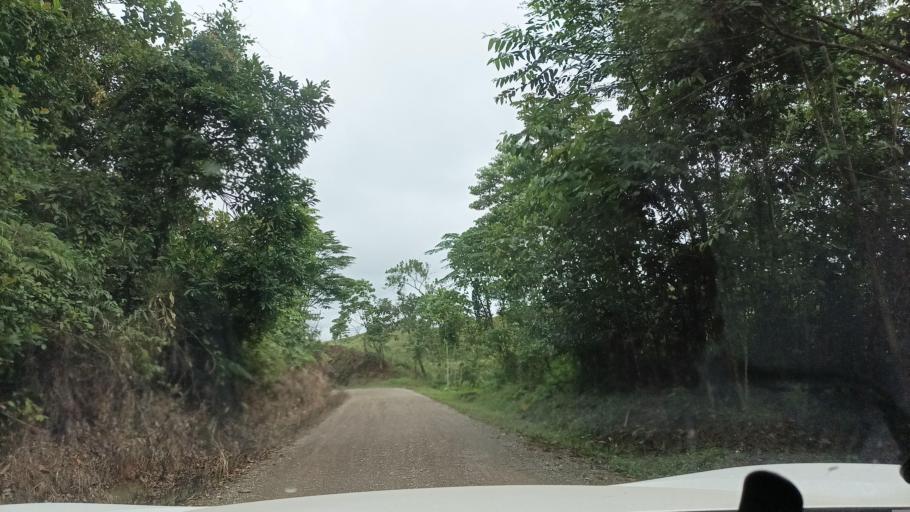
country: MX
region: Veracruz
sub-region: Uxpanapa
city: Poblado 10
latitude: 17.4303
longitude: -94.4198
